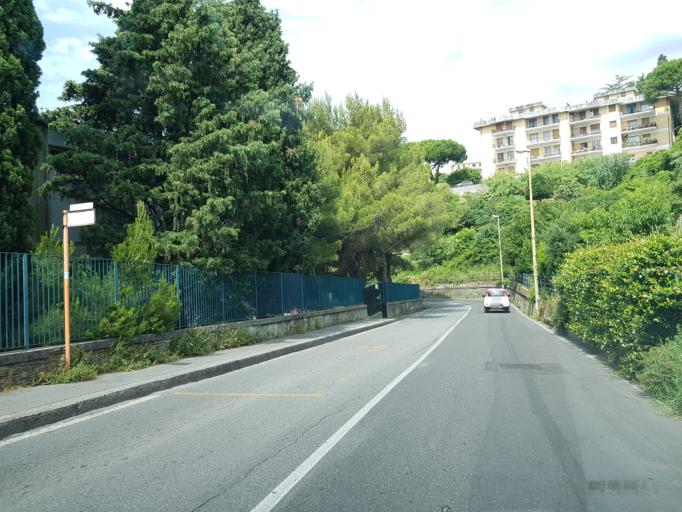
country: IT
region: Liguria
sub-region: Provincia di Genova
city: San Teodoro
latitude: 44.4322
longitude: 8.8452
